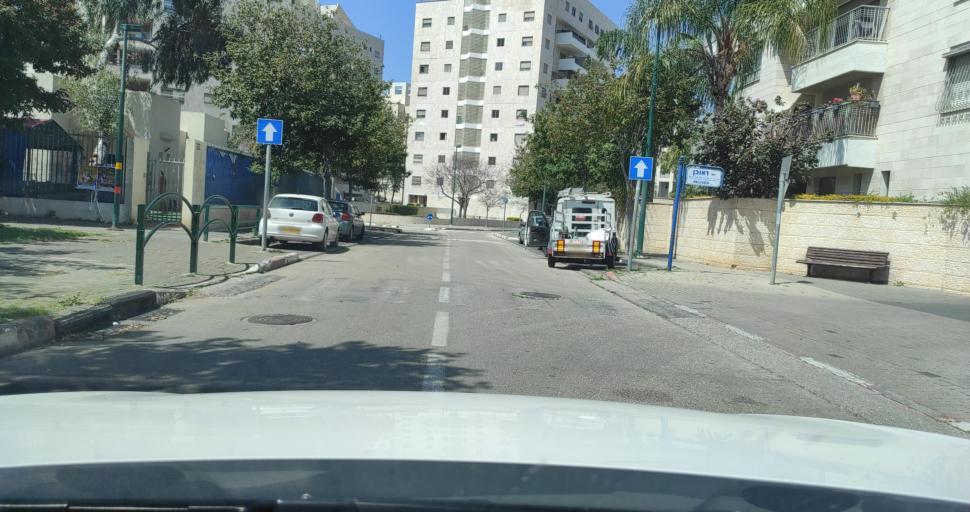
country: IL
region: Central District
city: Nordiyya
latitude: 32.3019
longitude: 34.8720
